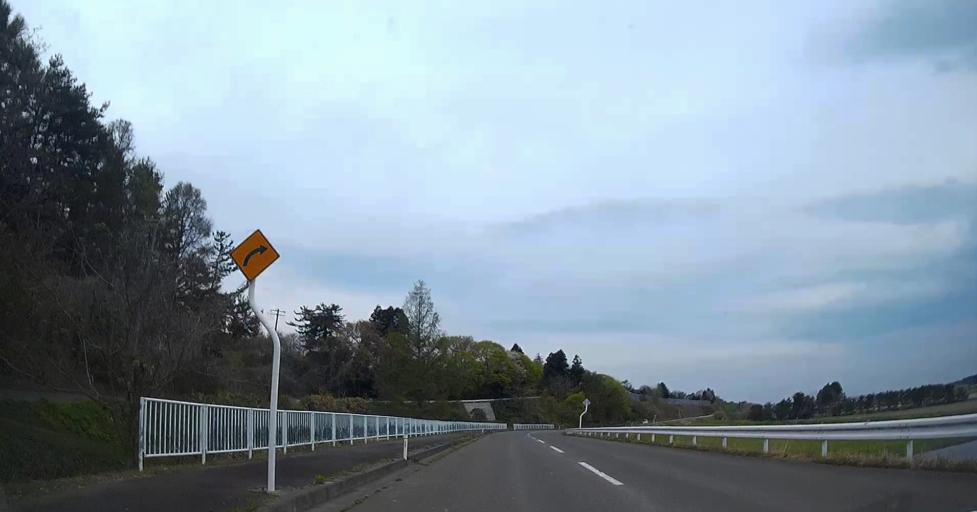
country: JP
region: Aomori
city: Goshogawara
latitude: 40.8993
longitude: 140.4908
